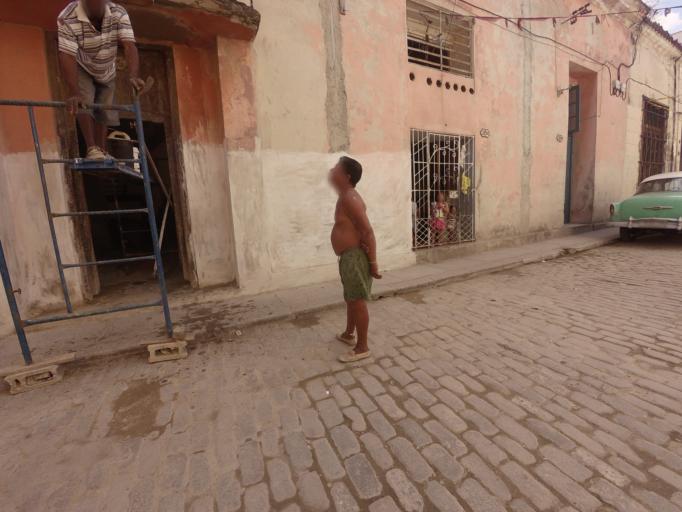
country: CU
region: La Habana
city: La Habana Vieja
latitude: 23.1304
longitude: -82.3512
